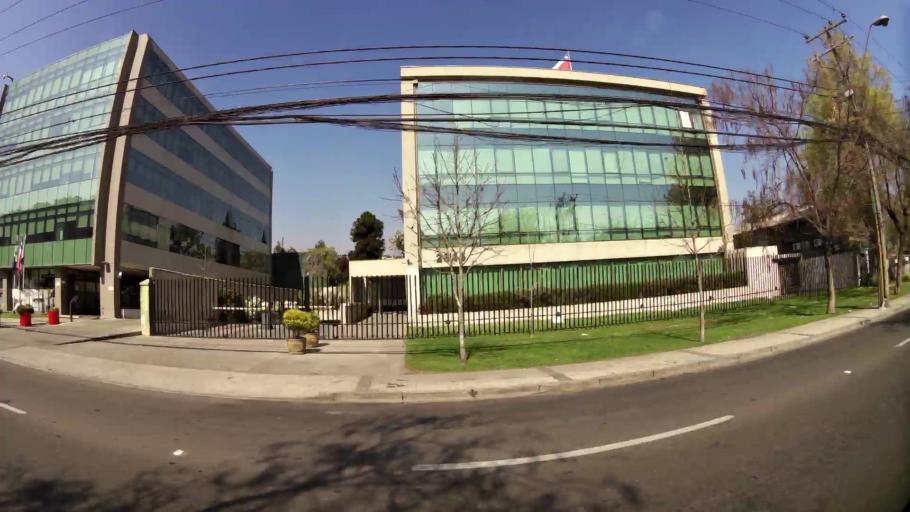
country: CL
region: Santiago Metropolitan
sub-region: Provincia de Santiago
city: Santiago
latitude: -33.4169
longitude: -70.6130
